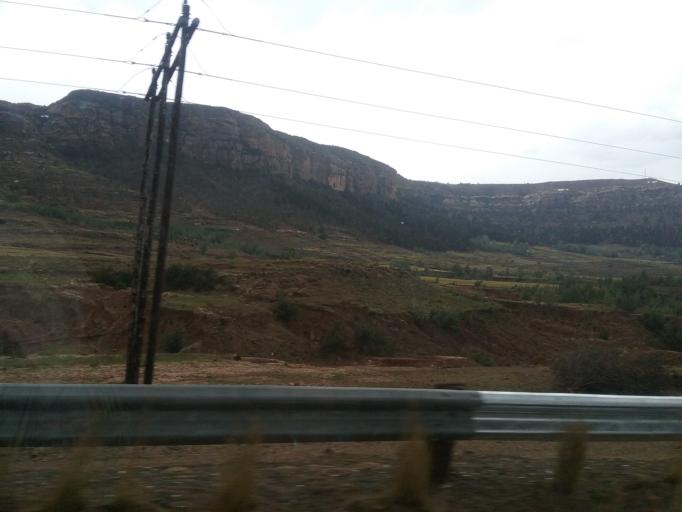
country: LS
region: Maseru
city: Nako
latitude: -29.4349
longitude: 27.6891
